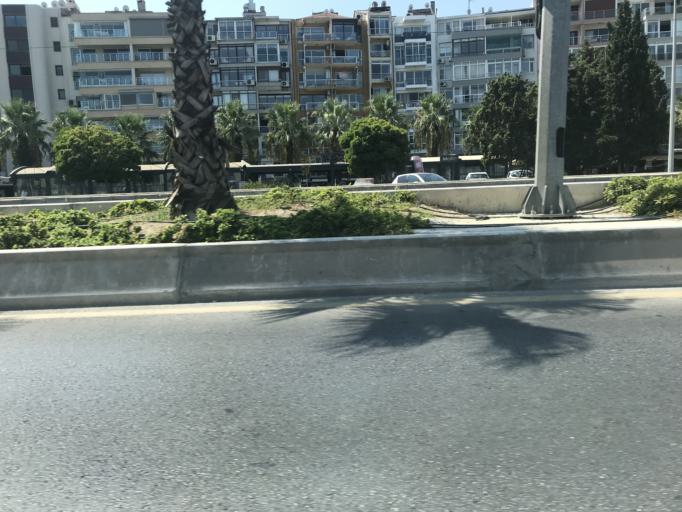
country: TR
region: Izmir
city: Izmir
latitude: 38.3984
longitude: 27.0856
